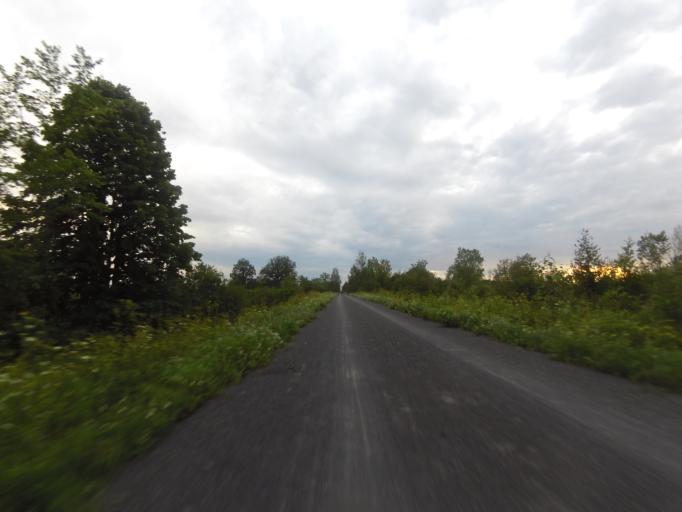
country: CA
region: Ontario
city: Carleton Place
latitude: 45.1841
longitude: -76.0381
